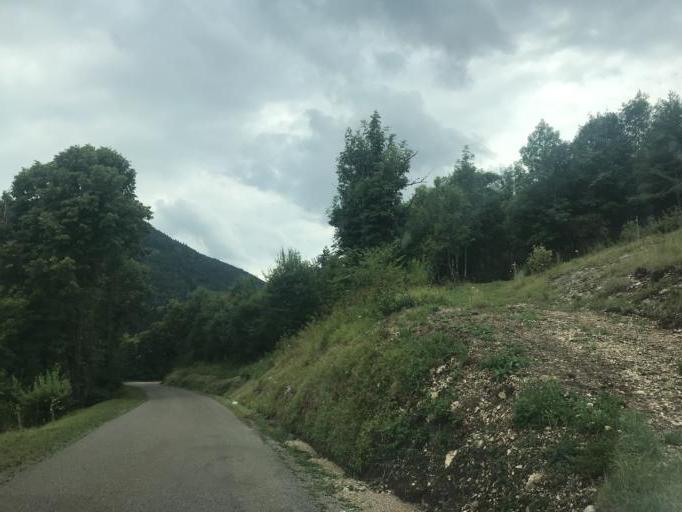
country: FR
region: Franche-Comte
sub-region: Departement du Jura
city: Saint-Claude
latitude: 46.3478
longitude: 5.8379
